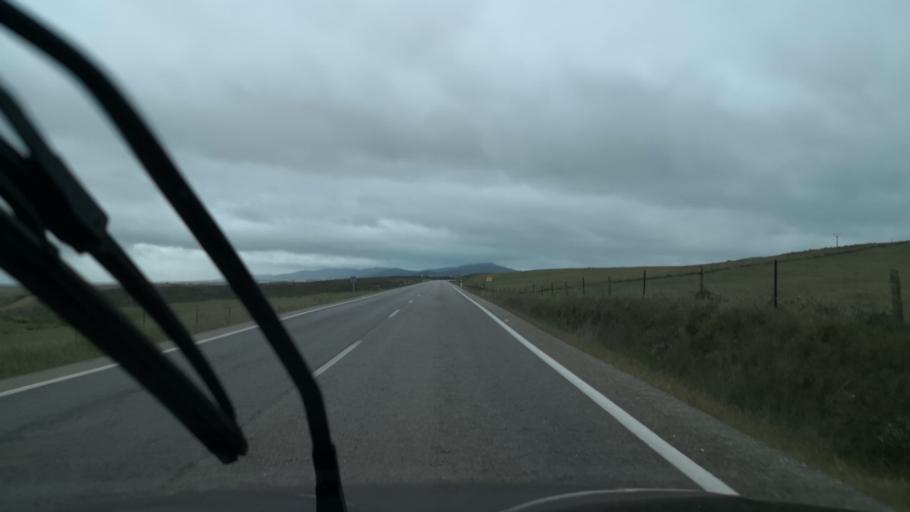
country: ES
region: Extremadura
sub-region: Provincia de Caceres
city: Casar de Caceres
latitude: 39.5283
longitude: -6.4014
